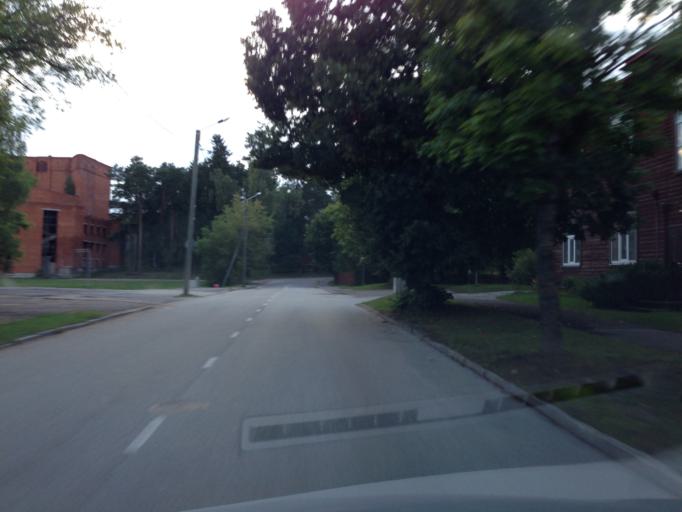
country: EE
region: Tartu
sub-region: Elva linn
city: Elva
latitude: 58.2254
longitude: 26.4193
